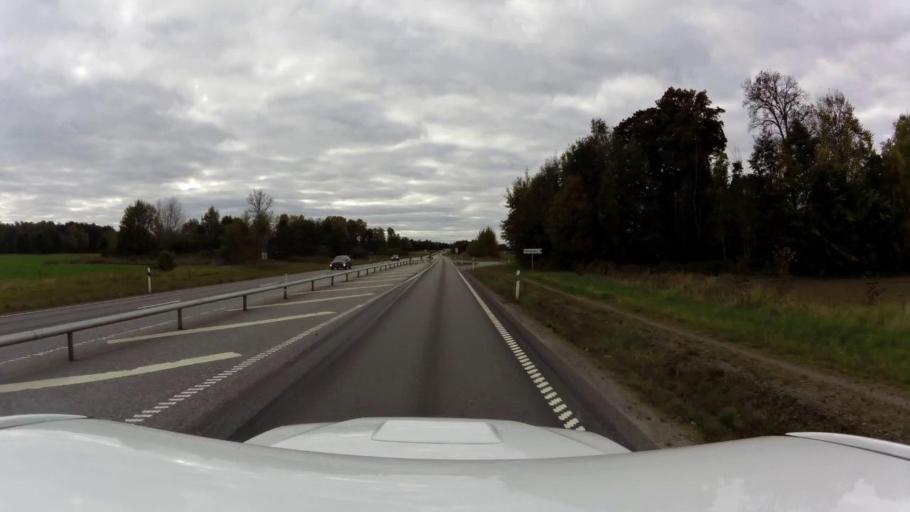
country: SE
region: OEstergoetland
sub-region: Linkopings Kommun
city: Malmslatt
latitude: 58.3720
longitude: 15.5435
